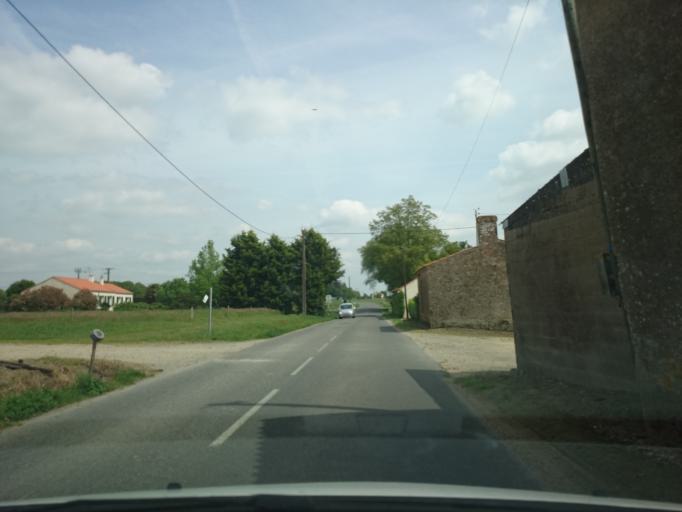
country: FR
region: Pays de la Loire
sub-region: Departement de la Loire-Atlantique
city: La Chevroliere
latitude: 47.0823
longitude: -1.5859
